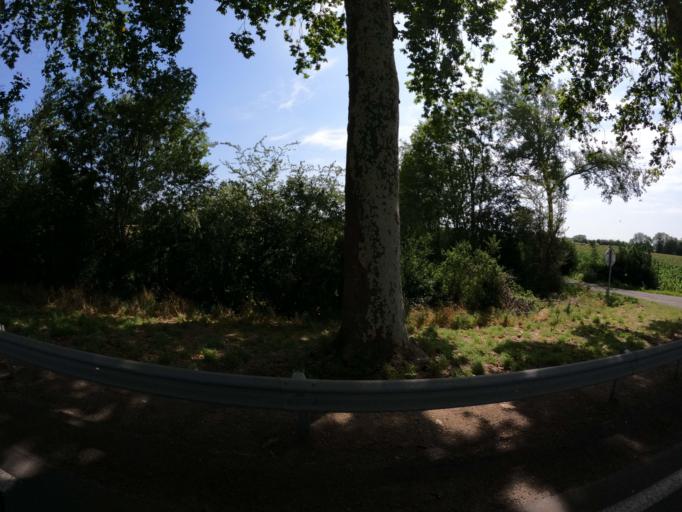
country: FR
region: Poitou-Charentes
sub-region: Departement des Deux-Sevres
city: Frontenay-Rohan-Rohan
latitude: 46.2748
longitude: -0.5256
